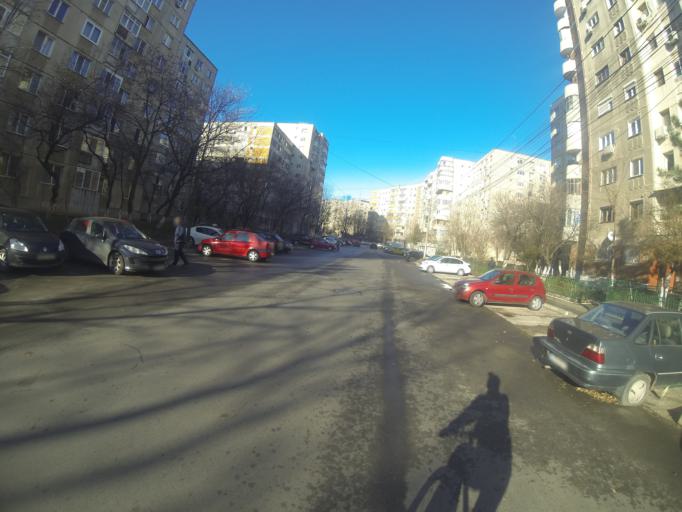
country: RO
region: Bucuresti
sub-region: Municipiul Bucuresti
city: Bucuresti
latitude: 44.4100
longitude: 26.0652
